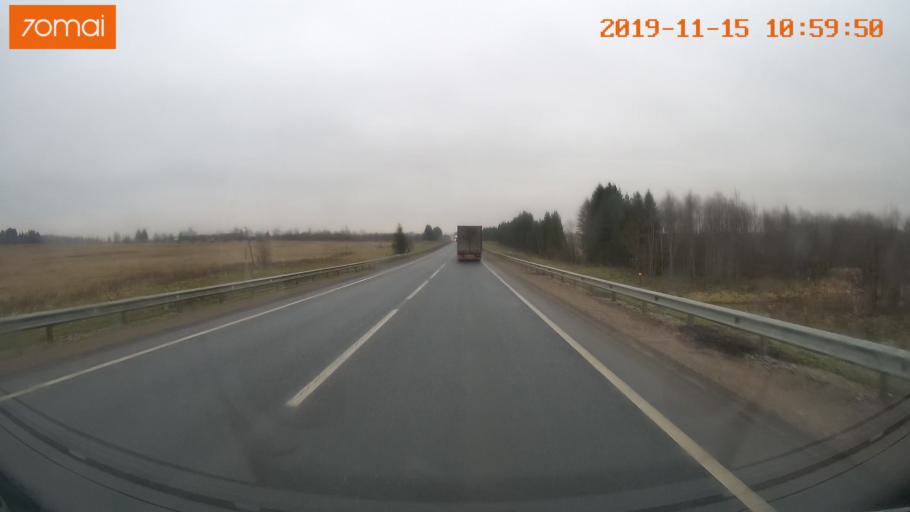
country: RU
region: Vologda
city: Chebsara
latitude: 59.1399
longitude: 38.8863
